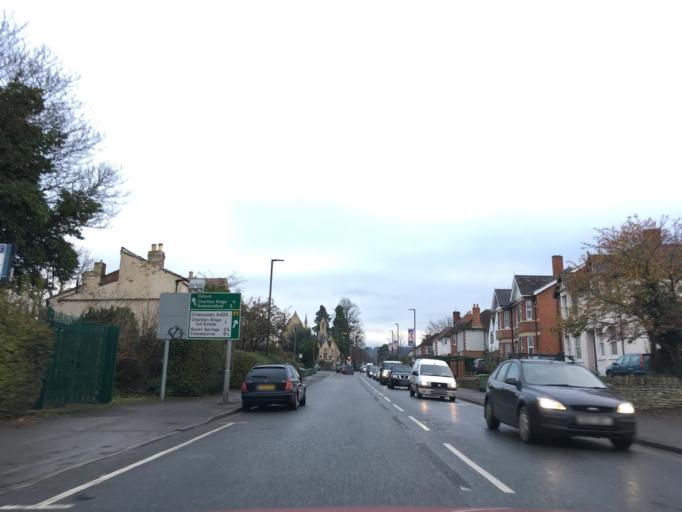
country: GB
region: England
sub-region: Gloucestershire
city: Charlton Kings
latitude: 51.8914
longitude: -2.0615
